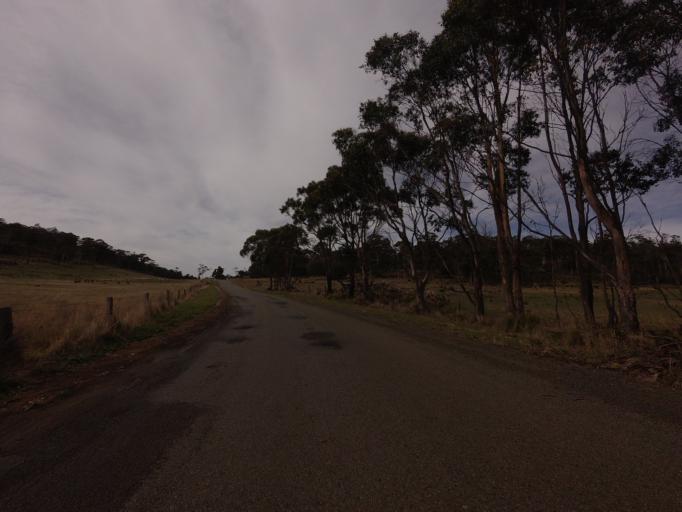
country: AU
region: Tasmania
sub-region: Sorell
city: Sorell
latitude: -42.5301
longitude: 147.6524
